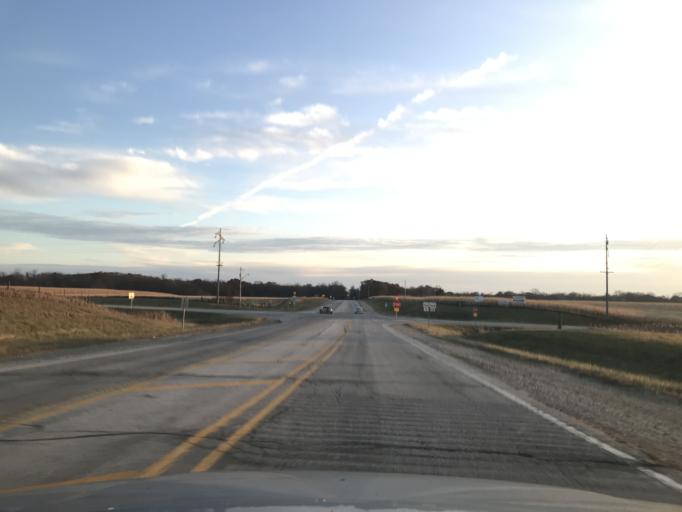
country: US
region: Illinois
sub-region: Henderson County
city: Oquawka
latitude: 40.9246
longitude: -90.8642
